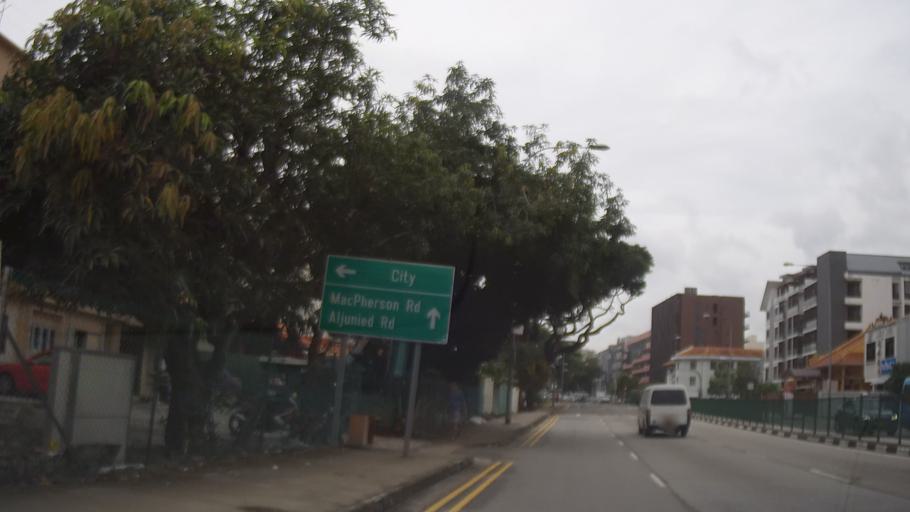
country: SG
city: Singapore
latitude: 1.3117
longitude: 103.8821
